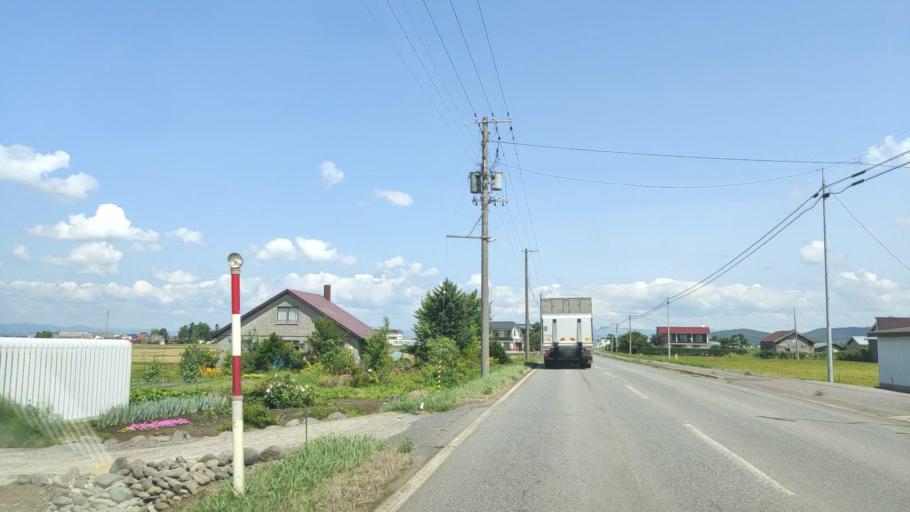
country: JP
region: Hokkaido
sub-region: Asahikawa-shi
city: Asahikawa
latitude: 43.7216
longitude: 142.4579
